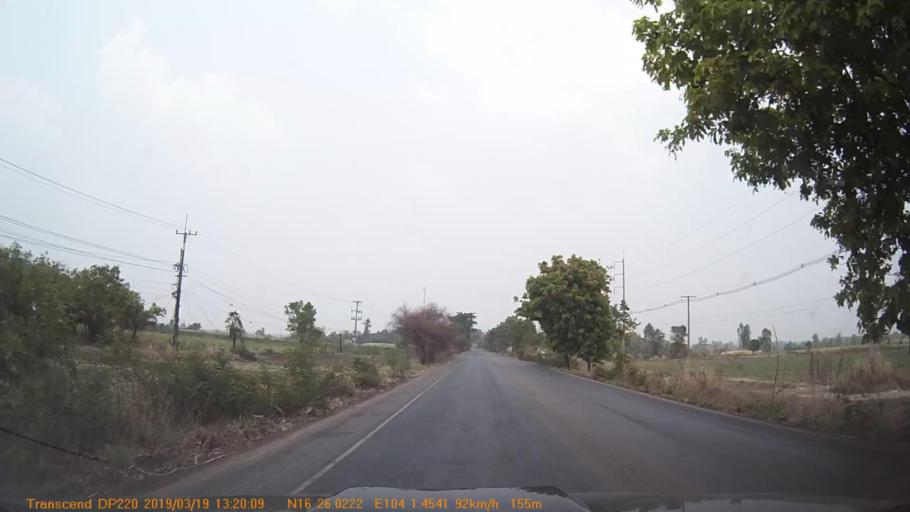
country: TH
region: Kalasin
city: Kuchinarai
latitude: 16.4341
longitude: 104.0244
